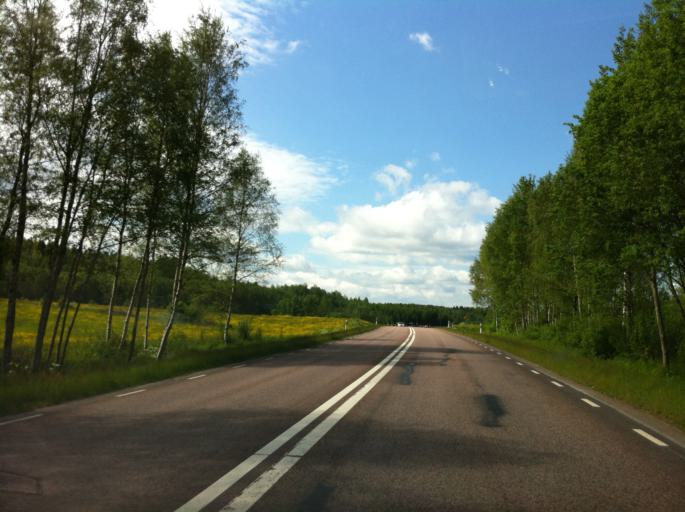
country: SE
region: Vaermland
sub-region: Karlstads Kommun
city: Valberg
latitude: 59.3763
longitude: 13.1548
